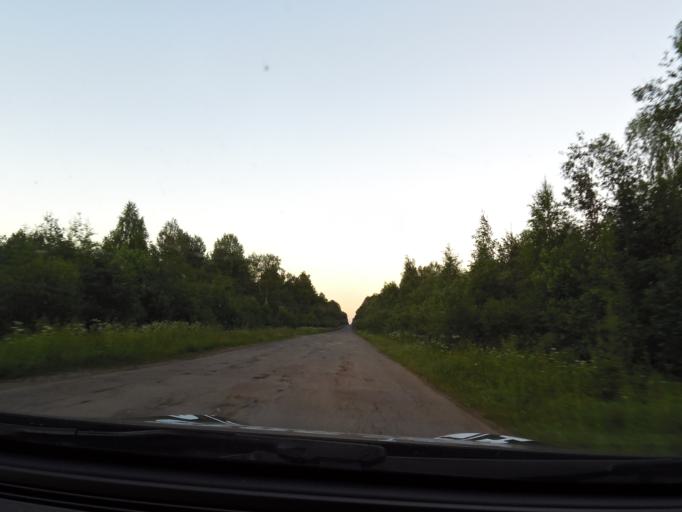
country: RU
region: Leningrad
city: Voznesen'ye
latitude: 60.8477
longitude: 35.5996
